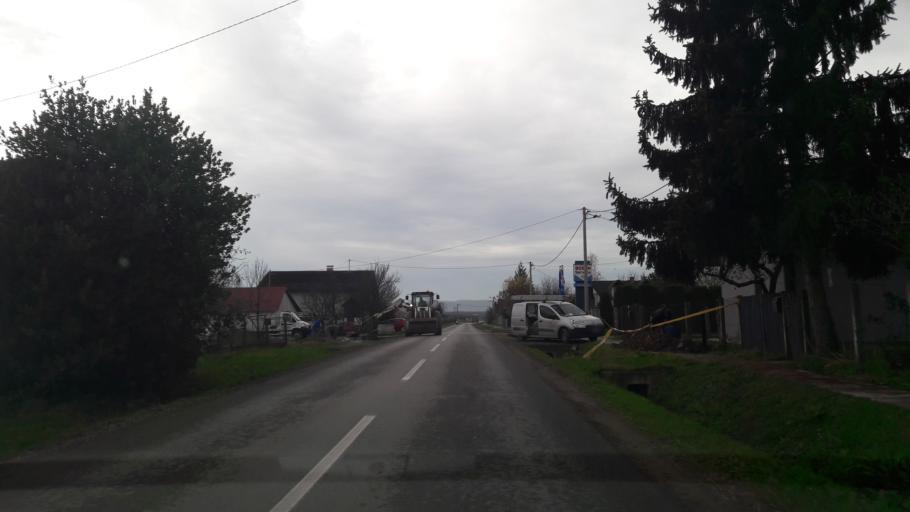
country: HR
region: Osjecko-Baranjska
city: Fericanci
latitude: 45.5305
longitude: 18.0200
